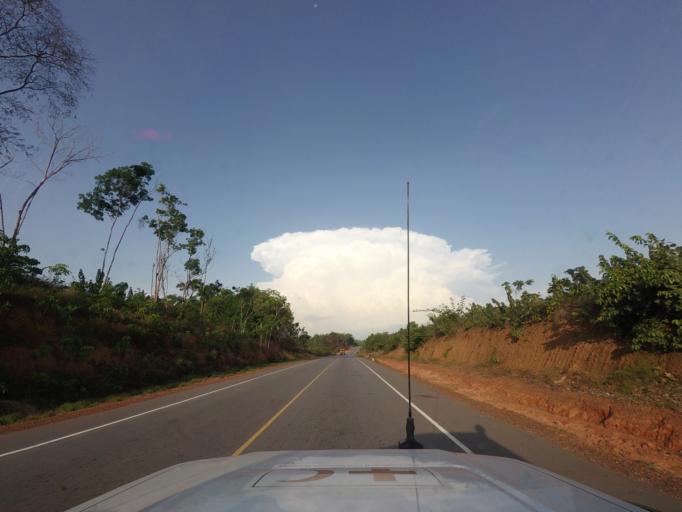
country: LR
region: Bong
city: Gbarnga
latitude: 7.0516
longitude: -9.2351
